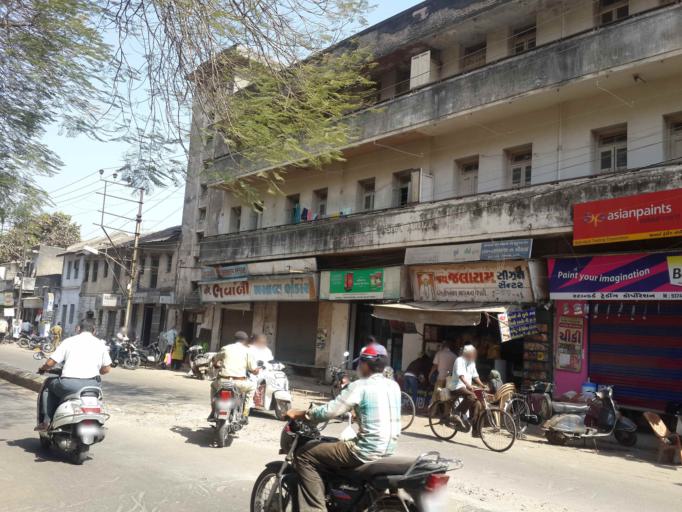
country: IN
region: Gujarat
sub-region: Rajkot
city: Rajkot
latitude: 22.3000
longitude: 70.8030
